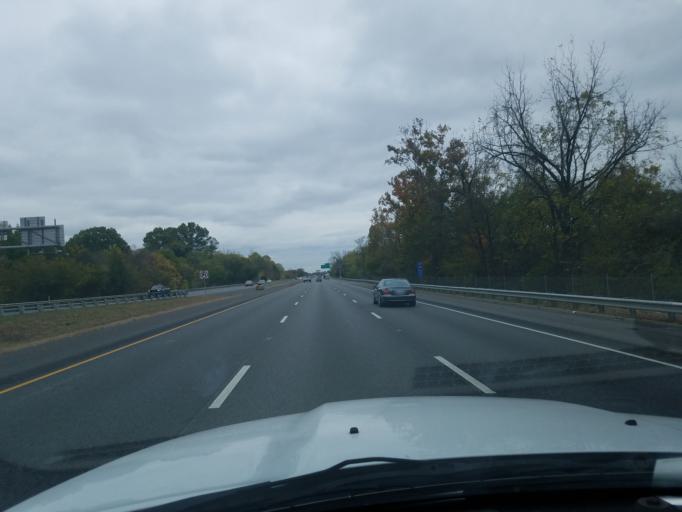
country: US
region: Indiana
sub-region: Floyd County
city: New Albany
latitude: 38.2949
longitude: -85.8402
